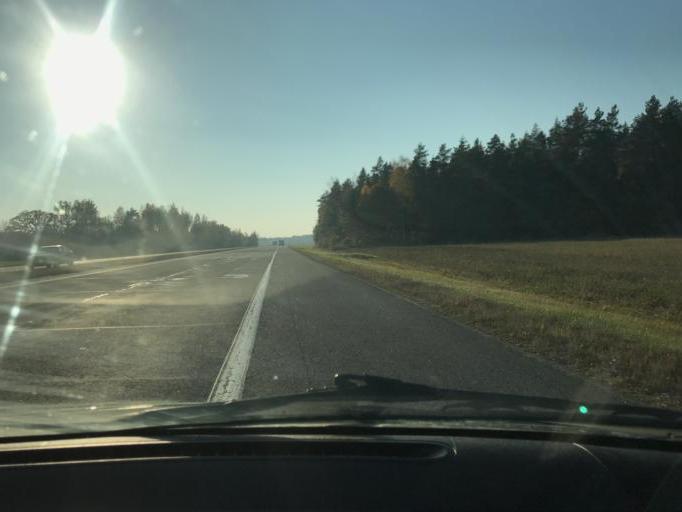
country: BY
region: Minsk
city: Krupki
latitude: 54.3163
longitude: 29.0483
